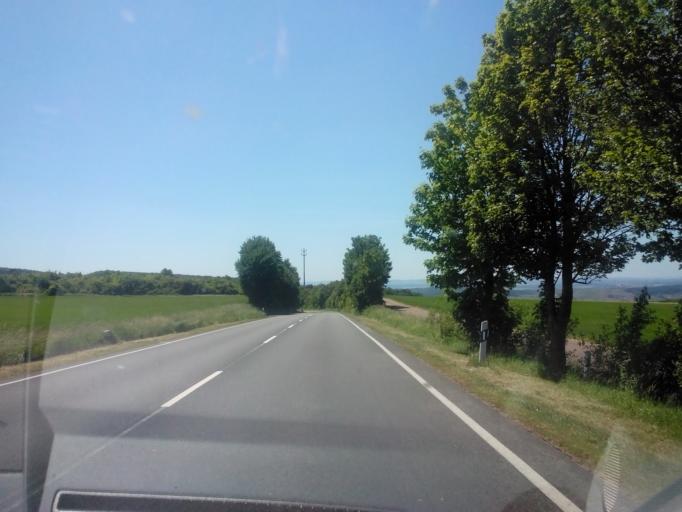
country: DE
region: Saarland
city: Perl
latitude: 49.4893
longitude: 6.4198
